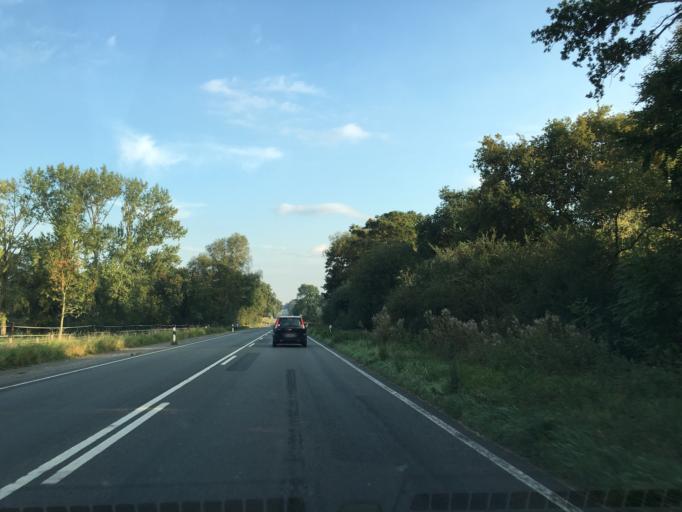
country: DE
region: North Rhine-Westphalia
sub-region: Regierungsbezirk Munster
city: Altenberge
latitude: 52.0313
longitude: 7.4841
